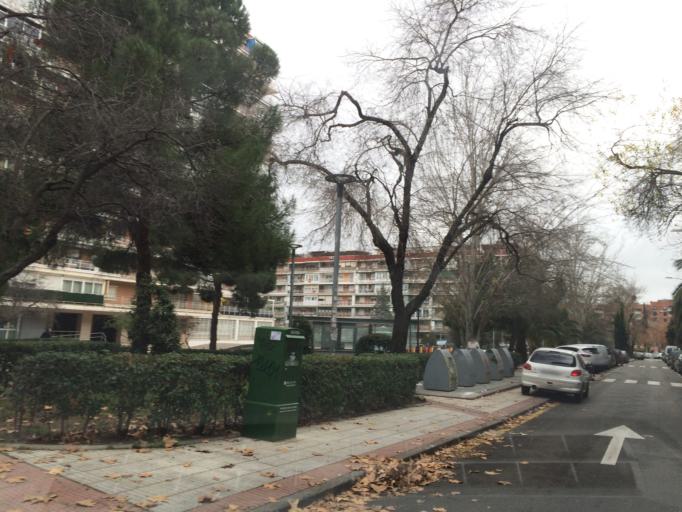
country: ES
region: Madrid
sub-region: Provincia de Madrid
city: Alcorcon
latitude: 40.3499
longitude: -3.8185
